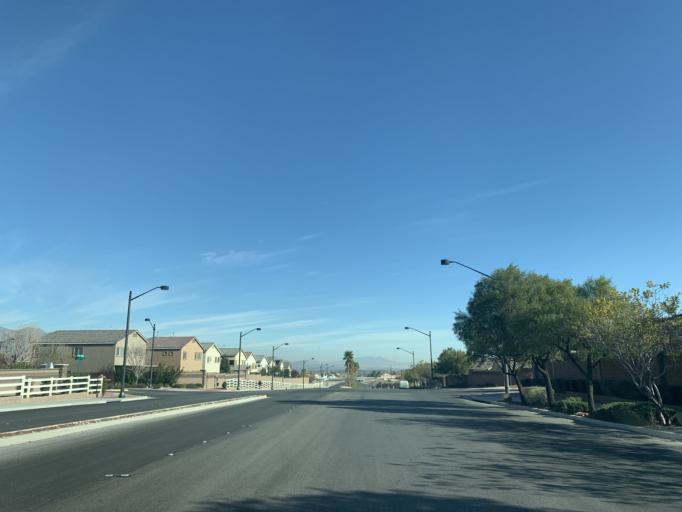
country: US
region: Nevada
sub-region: Clark County
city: Summerlin South
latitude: 36.3065
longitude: -115.2996
